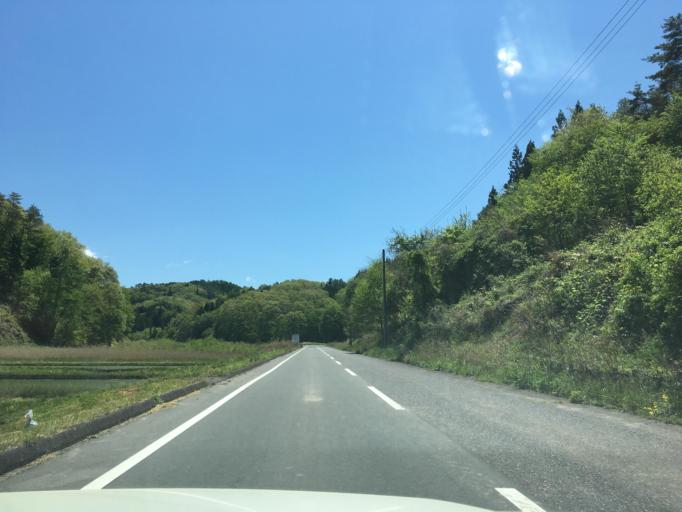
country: JP
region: Fukushima
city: Funehikimachi-funehiki
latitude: 37.3949
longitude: 140.6089
